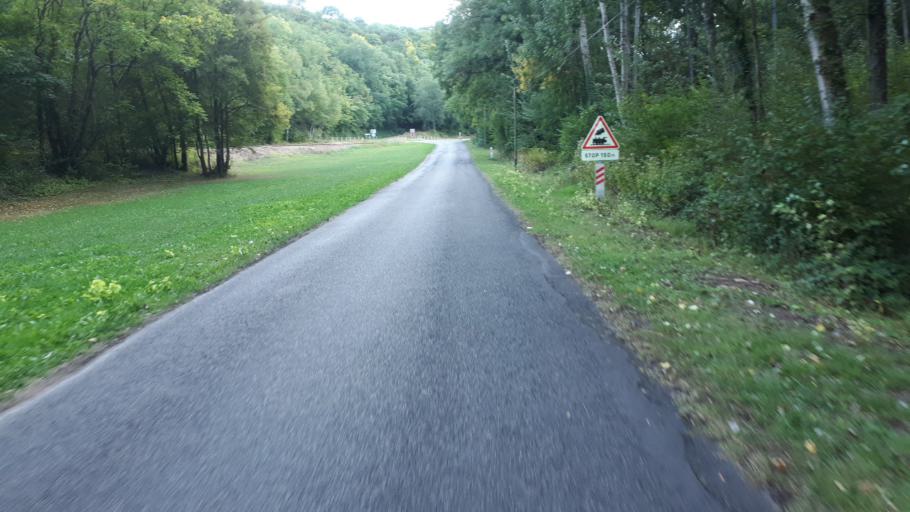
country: FR
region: Centre
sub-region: Departement du Loir-et-Cher
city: Villiers-sur-Loir
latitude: 47.7738
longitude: 0.9612
